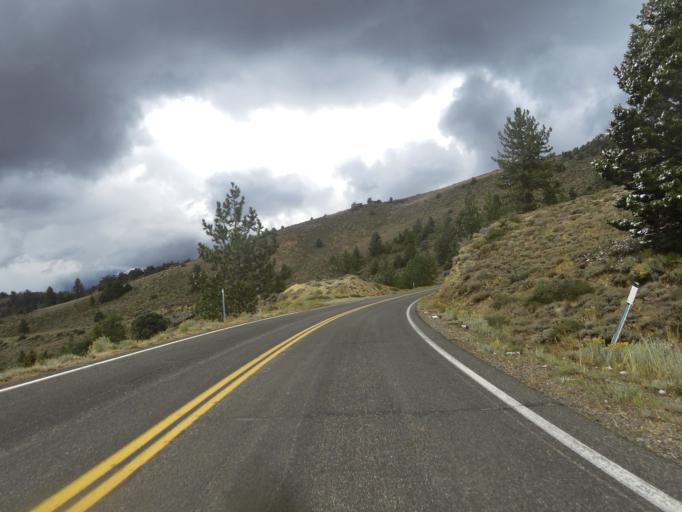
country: US
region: Nevada
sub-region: Douglas County
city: Gardnerville Ranchos
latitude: 38.6713
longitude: -119.6539
